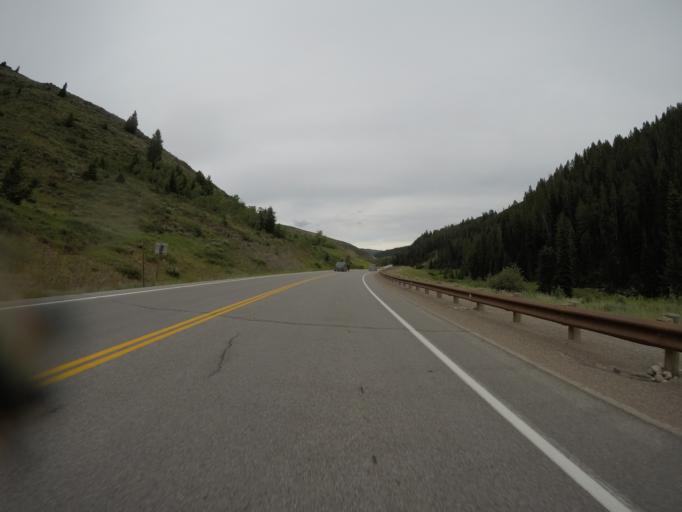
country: US
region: Wyoming
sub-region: Lincoln County
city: Afton
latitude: 42.4887
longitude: -110.9483
